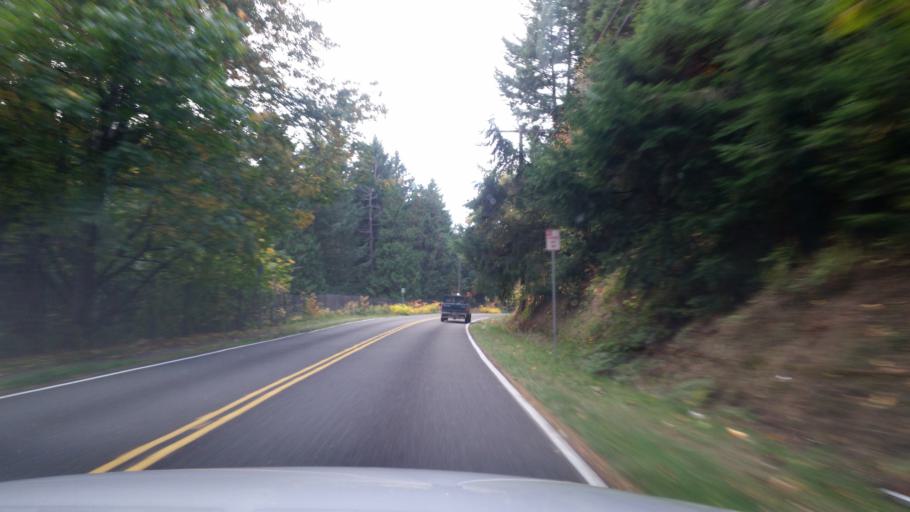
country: US
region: Washington
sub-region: King County
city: Shoreline
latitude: 47.7513
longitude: -122.3580
